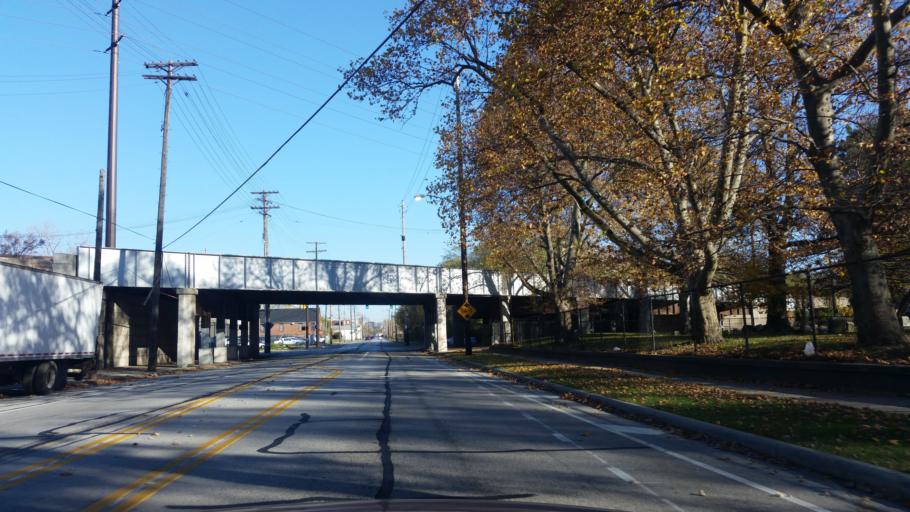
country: US
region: Ohio
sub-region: Cuyahoga County
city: Newburgh Heights
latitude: 41.4934
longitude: -81.6406
